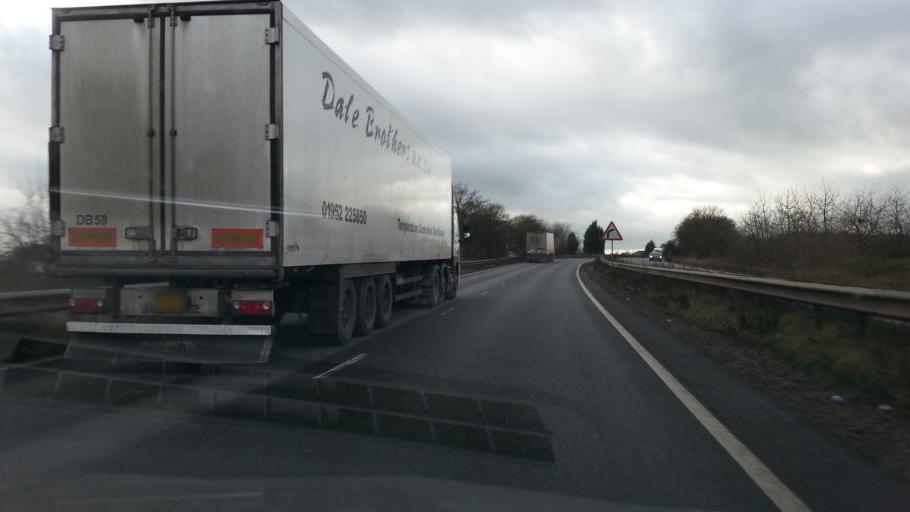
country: GB
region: England
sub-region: Staffordshire
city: Burton upon Trent
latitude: 52.8172
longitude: -1.6440
